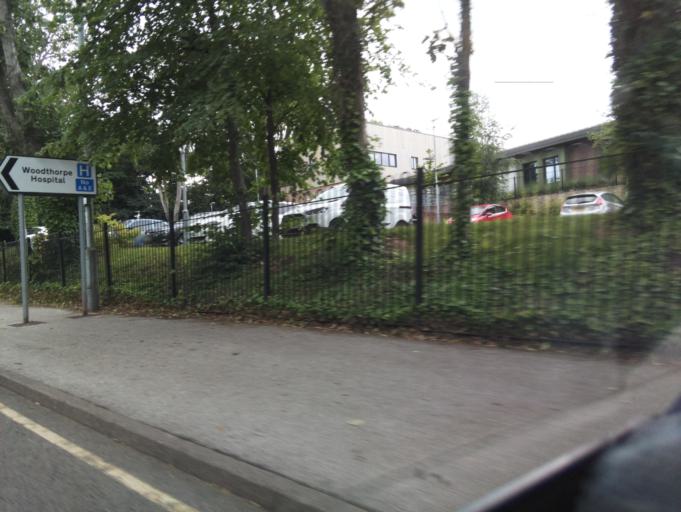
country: GB
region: England
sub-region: Nottinghamshire
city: Arnold
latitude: 52.9902
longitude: -1.1400
